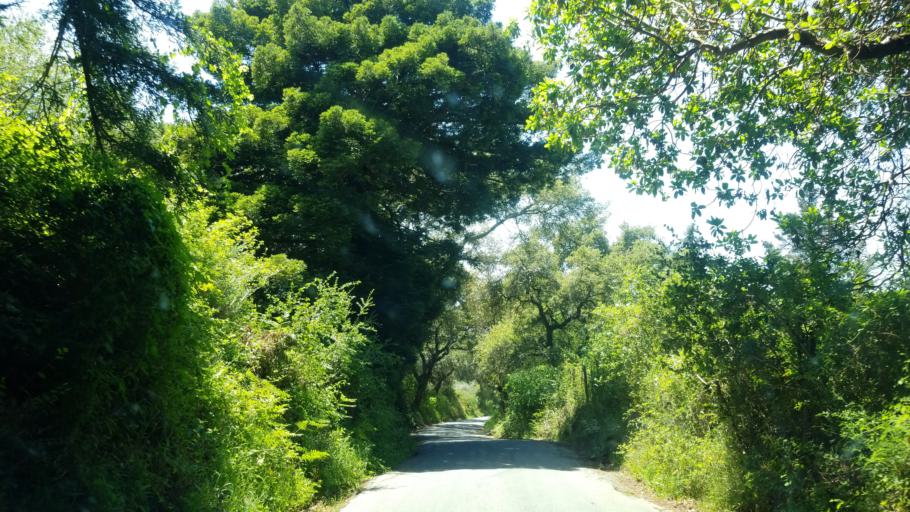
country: US
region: California
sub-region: Santa Cruz County
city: Interlaken
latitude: 37.0016
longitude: -121.7302
